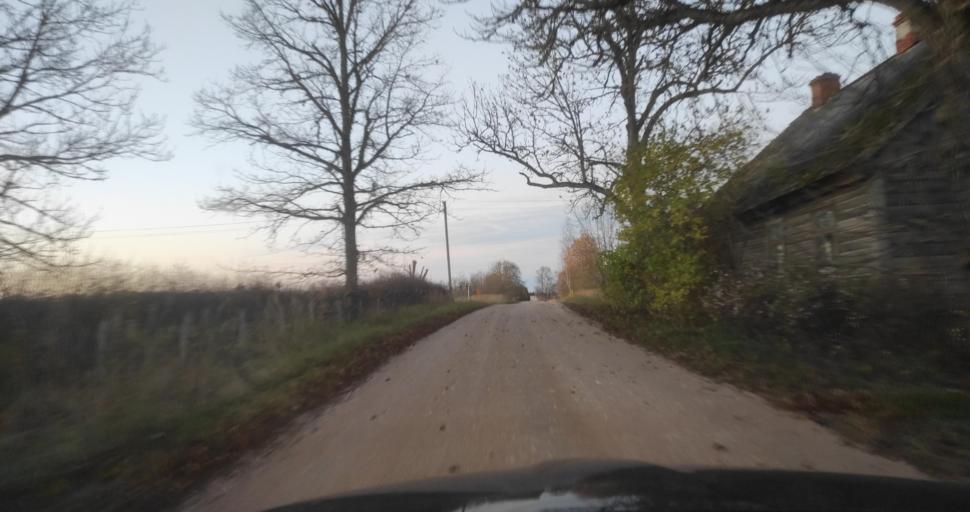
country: LV
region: Saldus Rajons
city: Saldus
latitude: 56.8042
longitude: 22.2848
